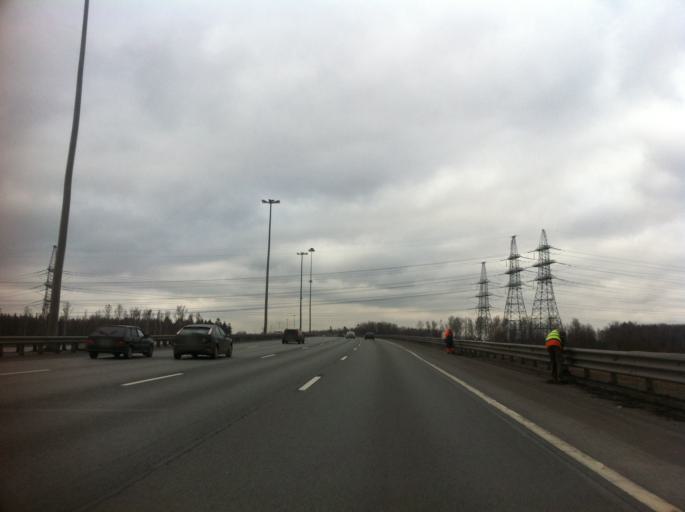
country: RU
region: St.-Petersburg
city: Krasnogvargeisky
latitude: 59.9276
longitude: 30.5336
